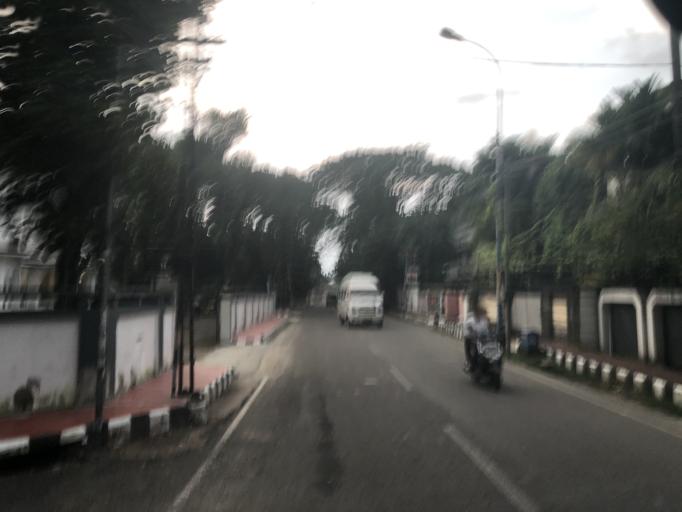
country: IN
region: Kerala
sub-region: Ernakulam
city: Cochin
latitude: 9.9520
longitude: 76.2563
